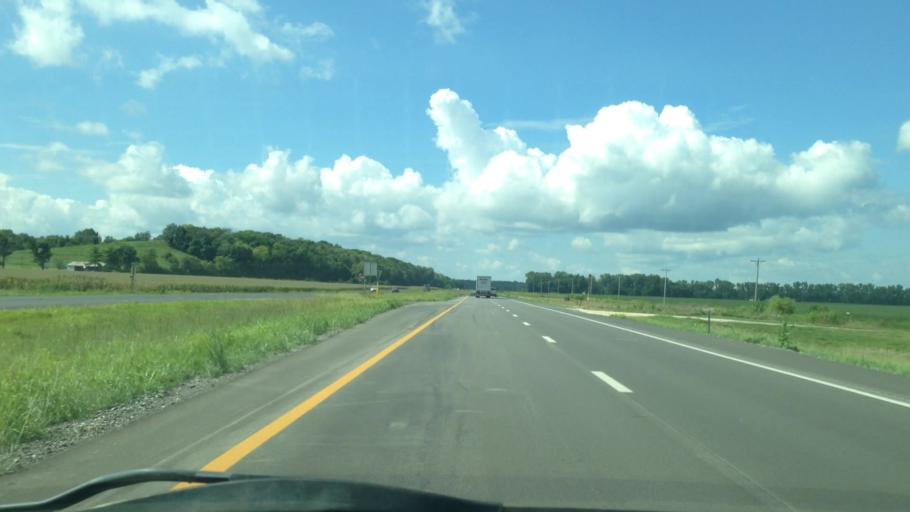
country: US
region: Illinois
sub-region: Adams County
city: Quincy
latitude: 39.9713
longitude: -91.5194
